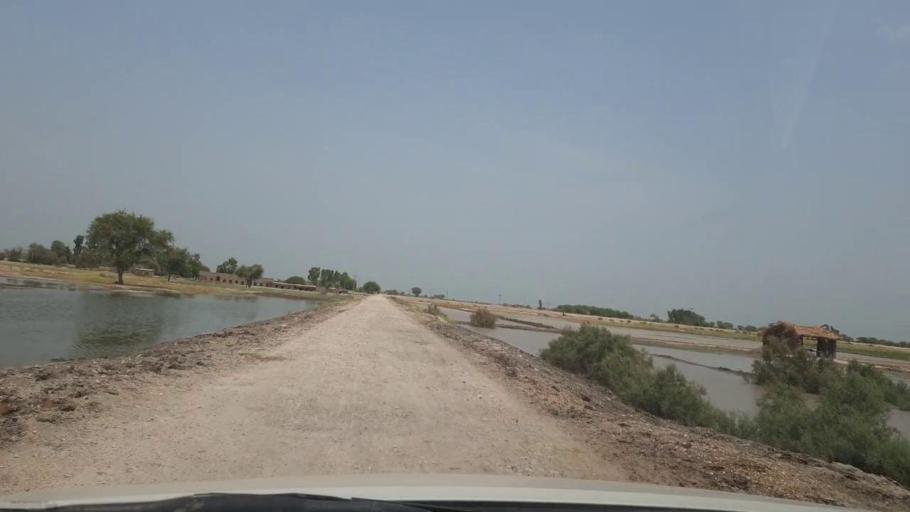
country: PK
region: Sindh
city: Rustam jo Goth
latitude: 28.0755
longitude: 68.8179
